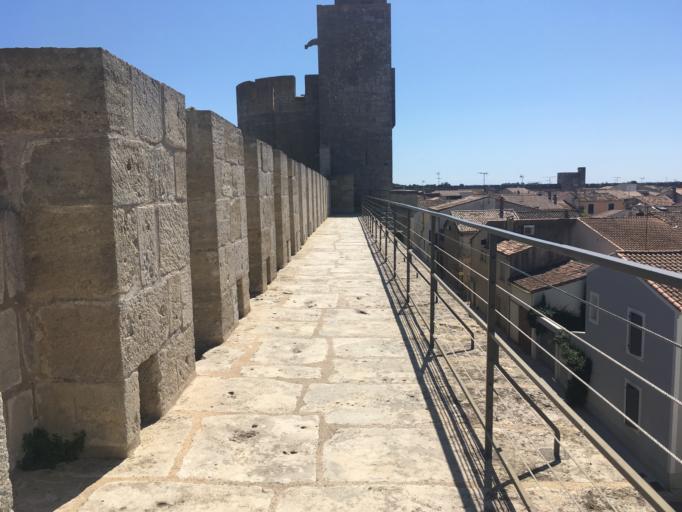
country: FR
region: Languedoc-Roussillon
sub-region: Departement du Gard
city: Aigues-Mortes
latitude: 43.5652
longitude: 4.1947
